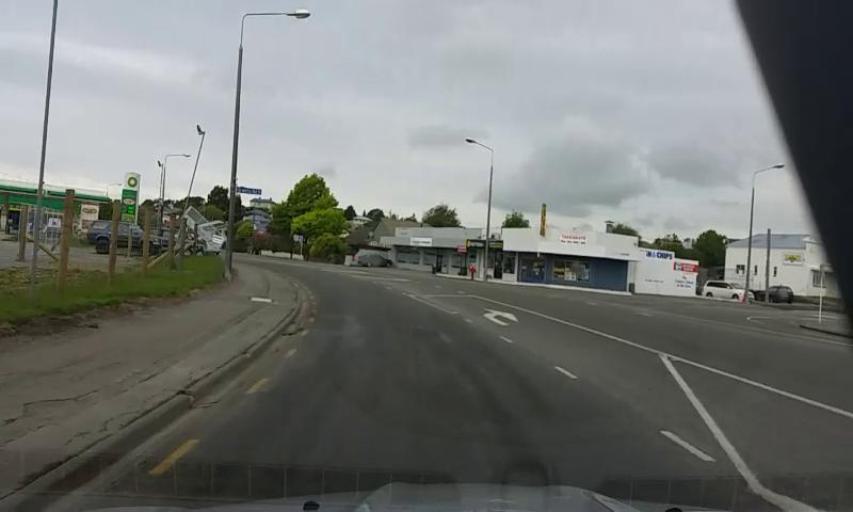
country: NZ
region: Canterbury
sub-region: Timaru District
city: Timaru
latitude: -44.3733
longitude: 171.2414
